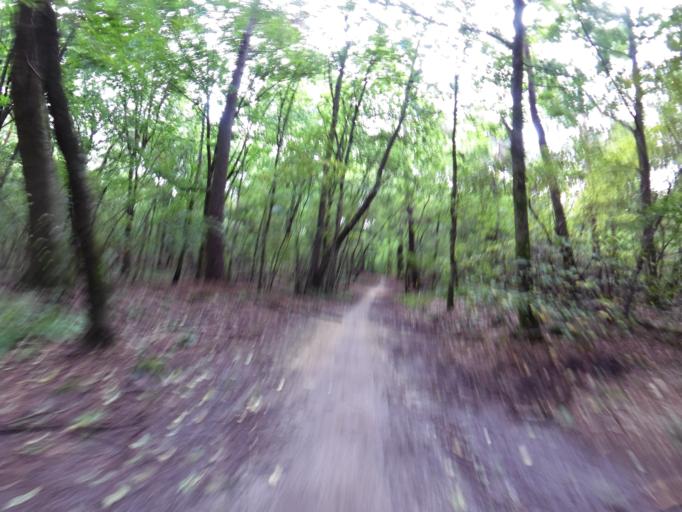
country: NL
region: North Brabant
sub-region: Gemeente Loon op Zand
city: Loon op Zand
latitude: 51.6338
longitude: 5.0657
